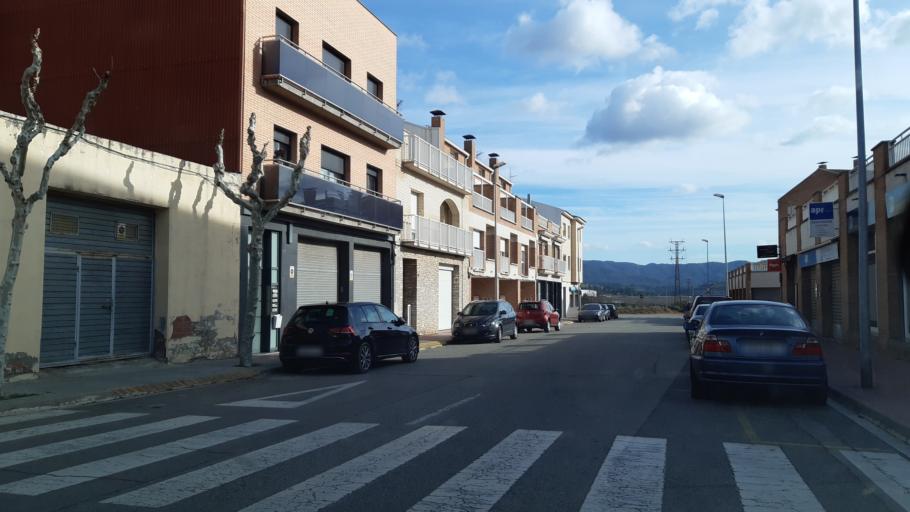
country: ES
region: Catalonia
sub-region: Provincia de Barcelona
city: Vilanova del Cami
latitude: 41.5694
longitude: 1.6427
